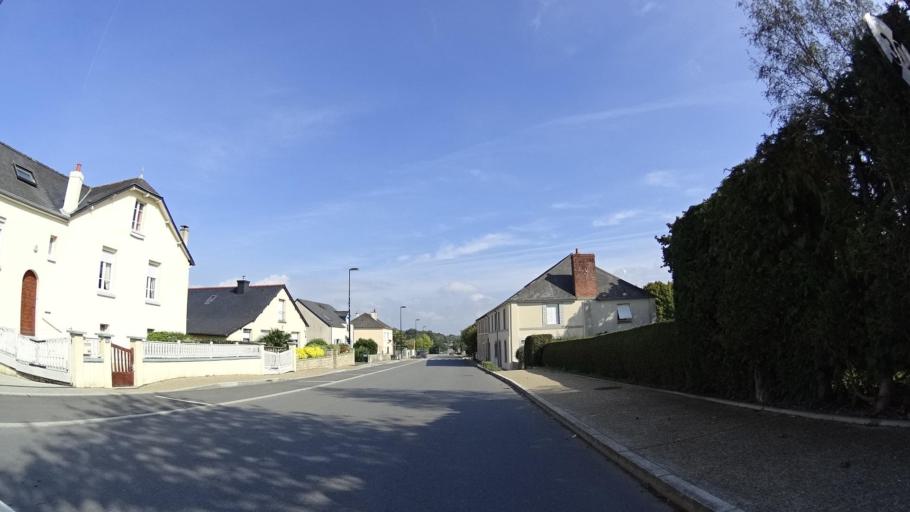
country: FR
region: Brittany
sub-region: Departement d'Ille-et-Vilaine
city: Medreac
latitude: 48.2679
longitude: -2.0613
